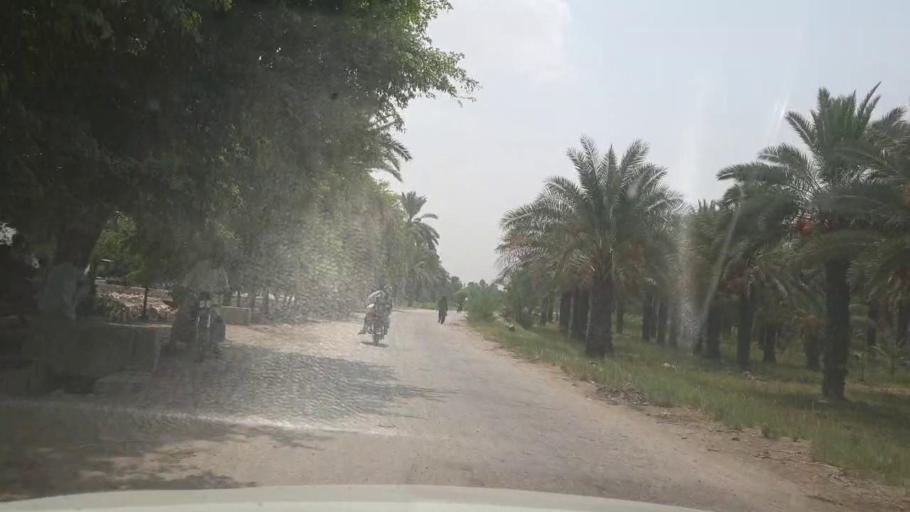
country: PK
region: Sindh
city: Kot Diji
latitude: 27.3726
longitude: 68.7200
